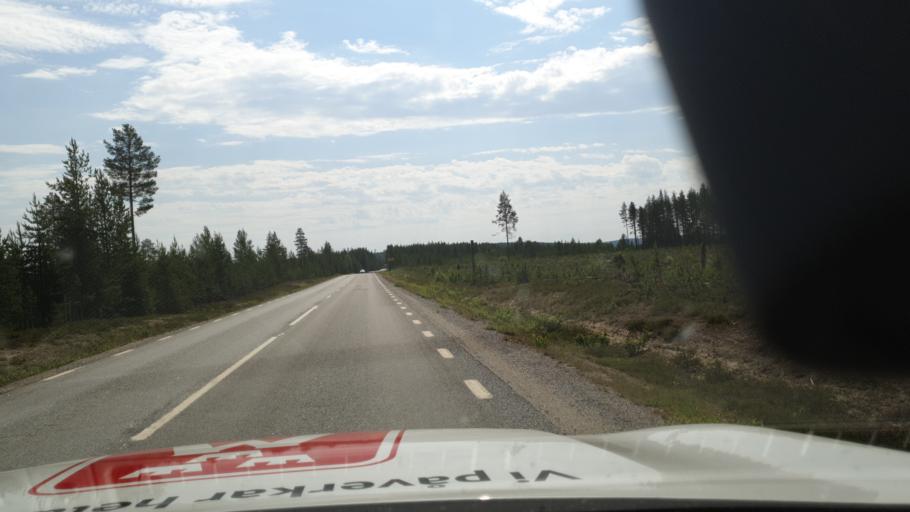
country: SE
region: Vaesterbotten
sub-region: Vindelns Kommun
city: Vindeln
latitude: 64.2376
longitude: 19.6957
